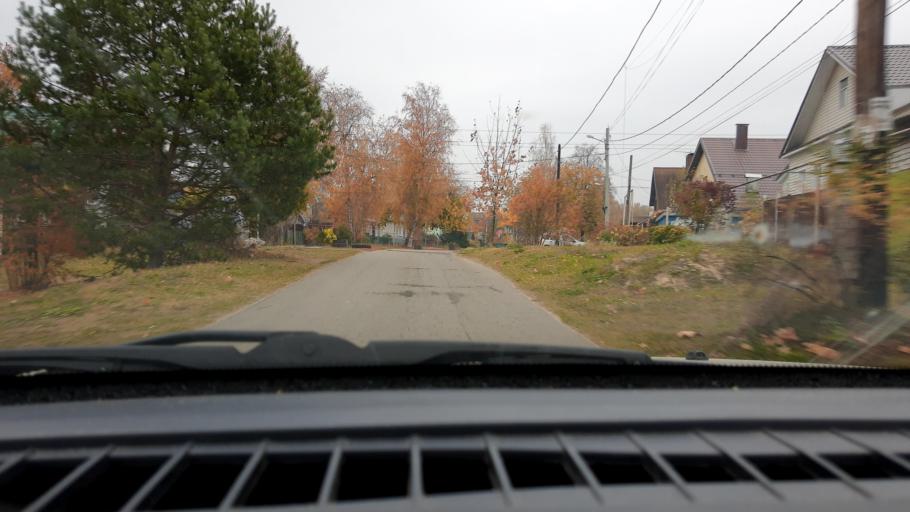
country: RU
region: Nizjnij Novgorod
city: Gorbatovka
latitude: 56.2100
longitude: 43.7598
